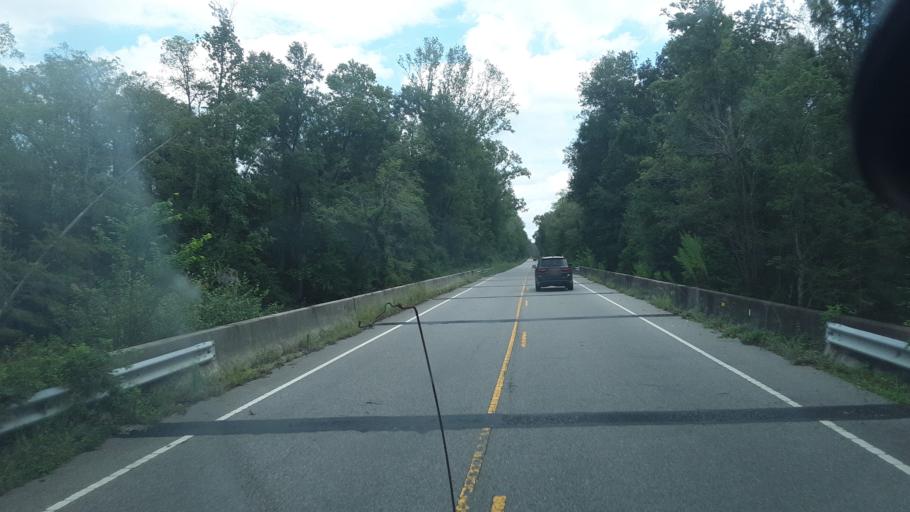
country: US
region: North Carolina
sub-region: Robeson County
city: Fairmont
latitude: 34.3463
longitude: -79.0753
